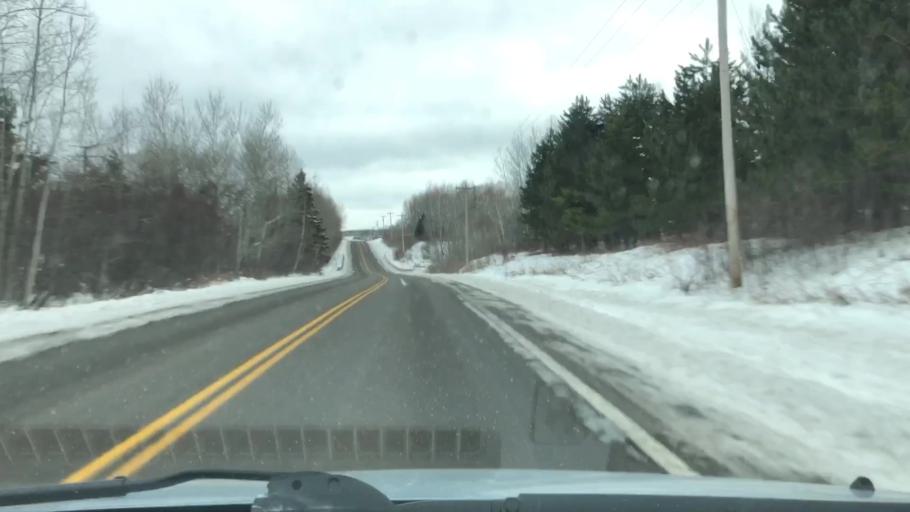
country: US
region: Minnesota
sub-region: Saint Louis County
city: Proctor
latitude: 46.7009
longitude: -92.2838
